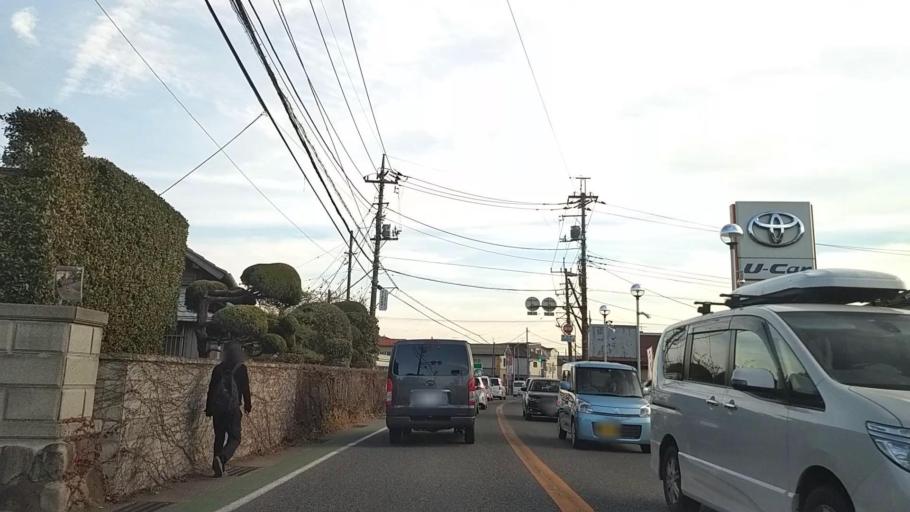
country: JP
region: Kanagawa
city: Atsugi
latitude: 35.4781
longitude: 139.3420
